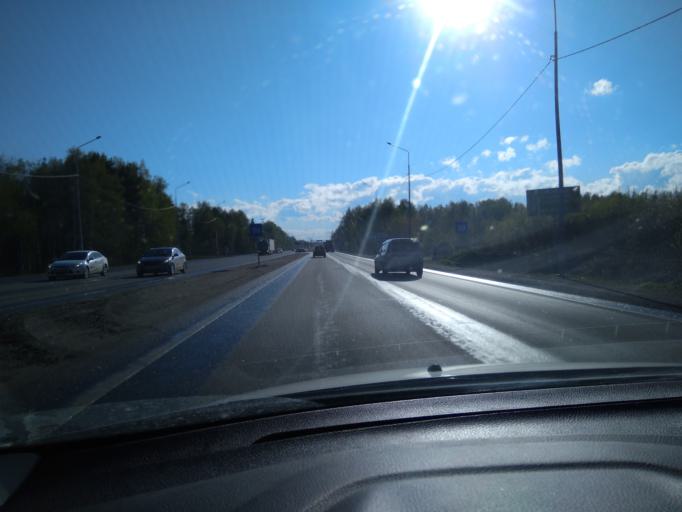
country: RU
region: Tjumen
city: Moskovskiy
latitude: 57.1167
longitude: 65.4272
